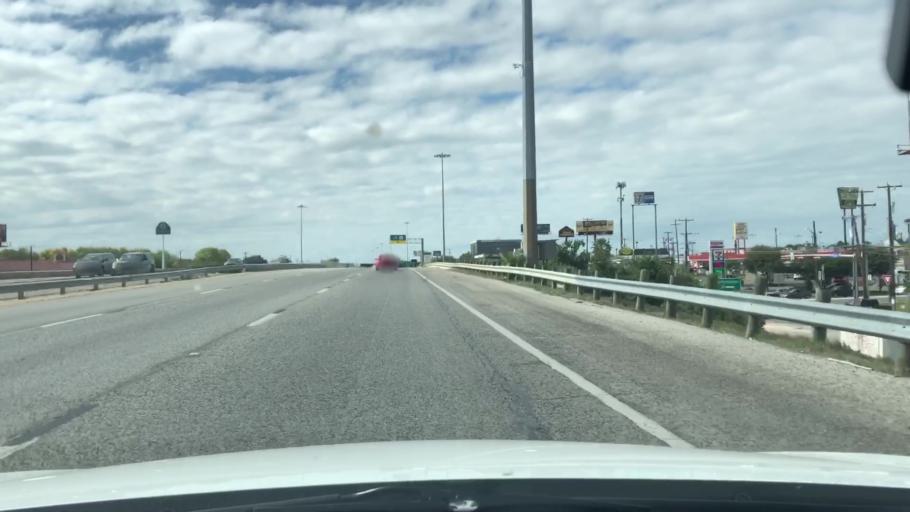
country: US
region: Texas
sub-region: Bexar County
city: Lackland Air Force Base
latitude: 29.4028
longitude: -98.6273
